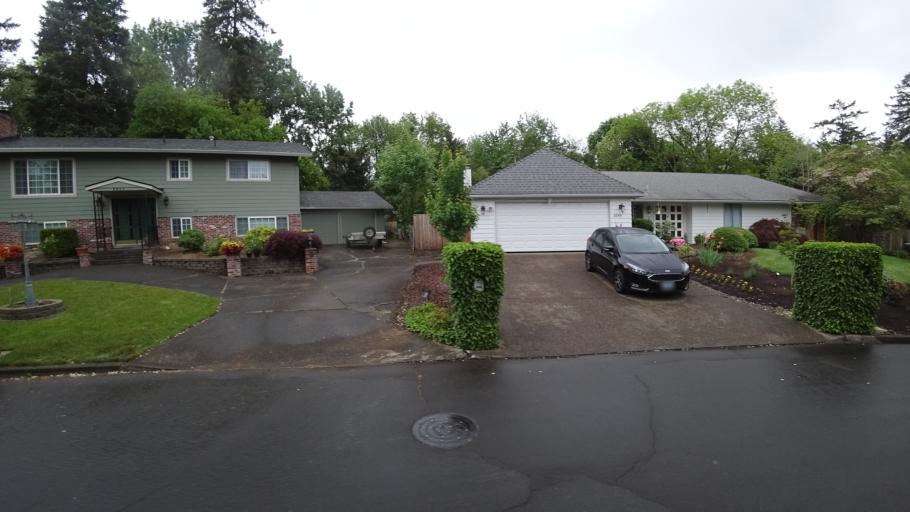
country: US
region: Oregon
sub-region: Washington County
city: Garden Home-Whitford
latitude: 45.4698
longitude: -122.7667
